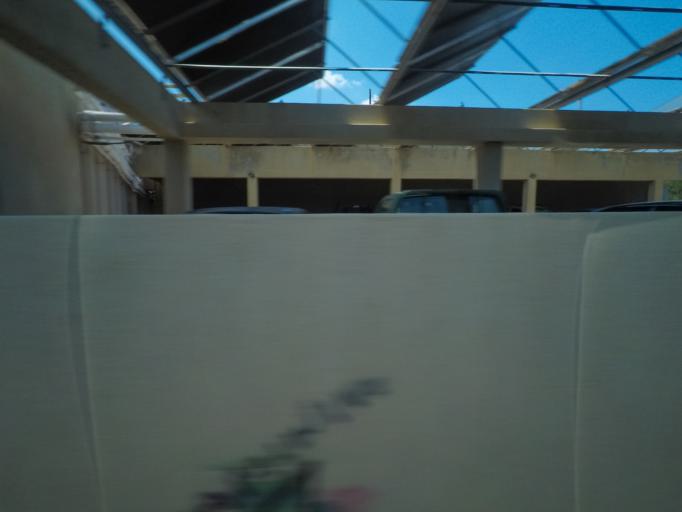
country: GR
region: Crete
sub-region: Nomos Lasithiou
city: Skhisma
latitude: 35.2448
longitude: 25.7298
